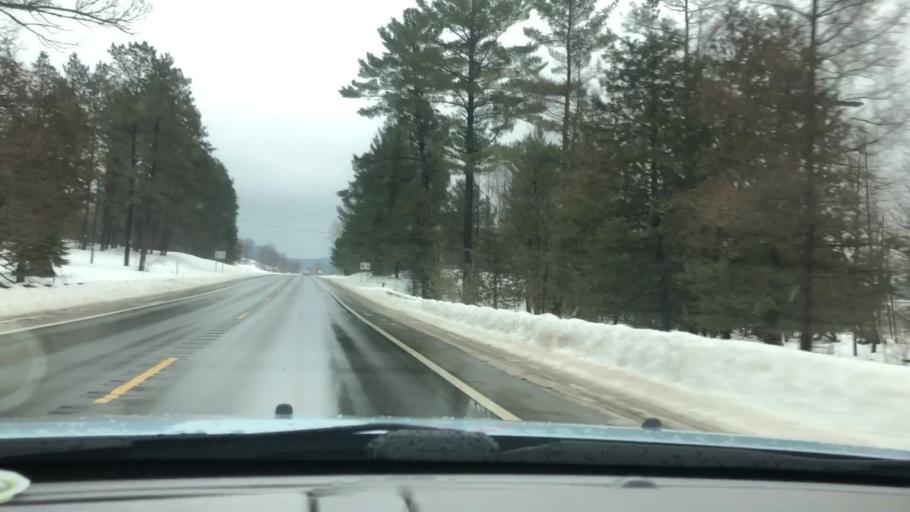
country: US
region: Michigan
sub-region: Charlevoix County
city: Boyne City
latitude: 45.0944
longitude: -84.9616
